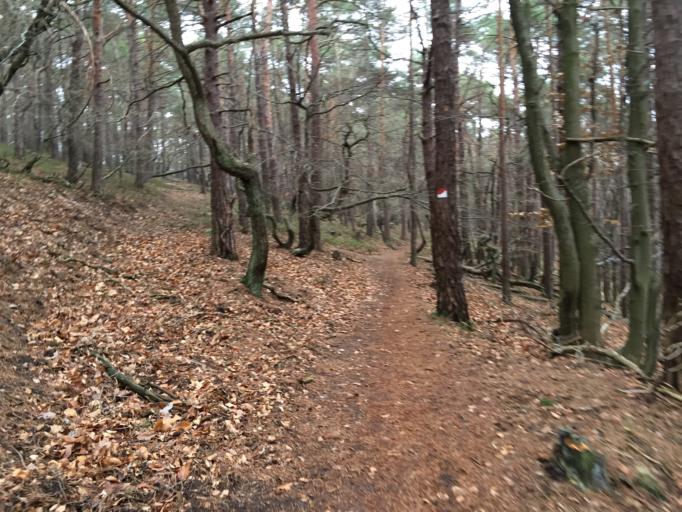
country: DE
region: Rheinland-Pfalz
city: Sankt Martin
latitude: 49.3324
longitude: 8.1096
